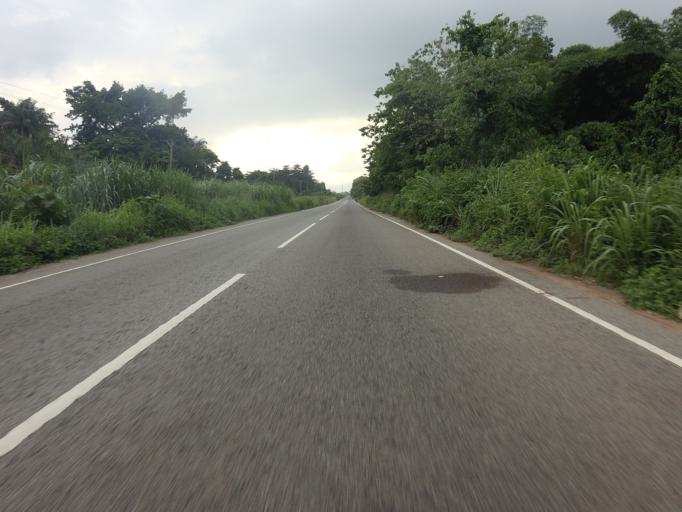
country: GH
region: Volta
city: Ho
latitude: 6.7766
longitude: 0.4735
